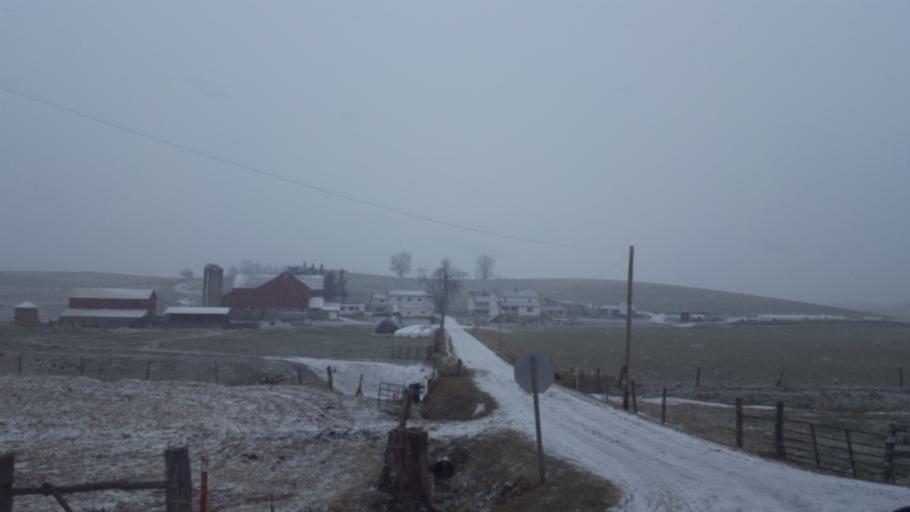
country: US
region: Ohio
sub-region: Tuscarawas County
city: Sugarcreek
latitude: 40.4634
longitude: -81.7394
